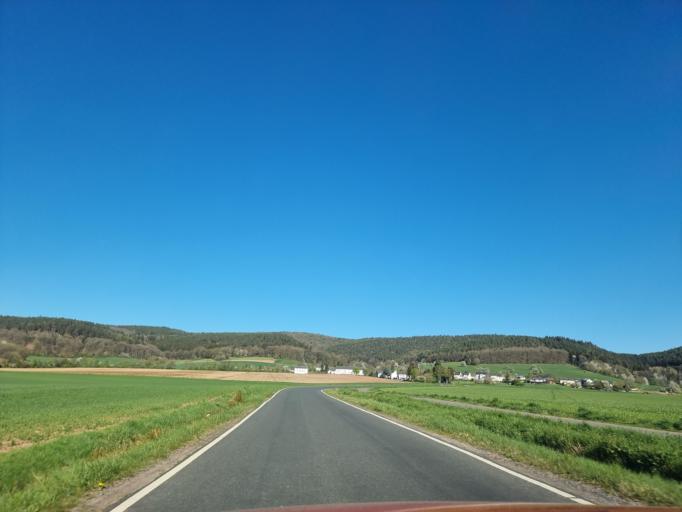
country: DE
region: Rheinland-Pfalz
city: Hetzerath
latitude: 49.8838
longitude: 6.7994
